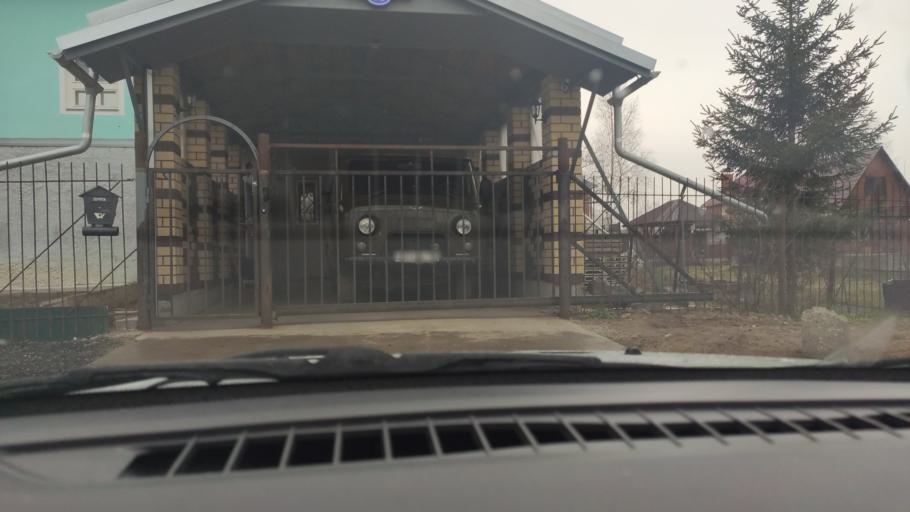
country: RU
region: Perm
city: Perm
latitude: 58.1126
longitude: 56.3956
